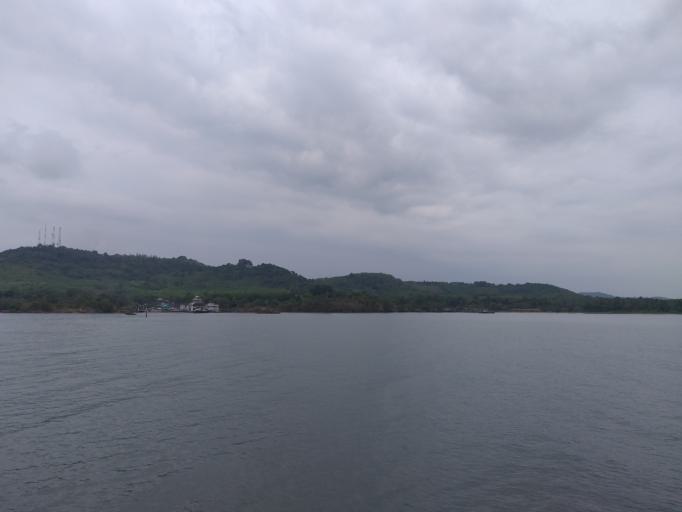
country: TH
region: Trat
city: Laem Ngop
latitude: 12.1812
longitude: 102.3016
